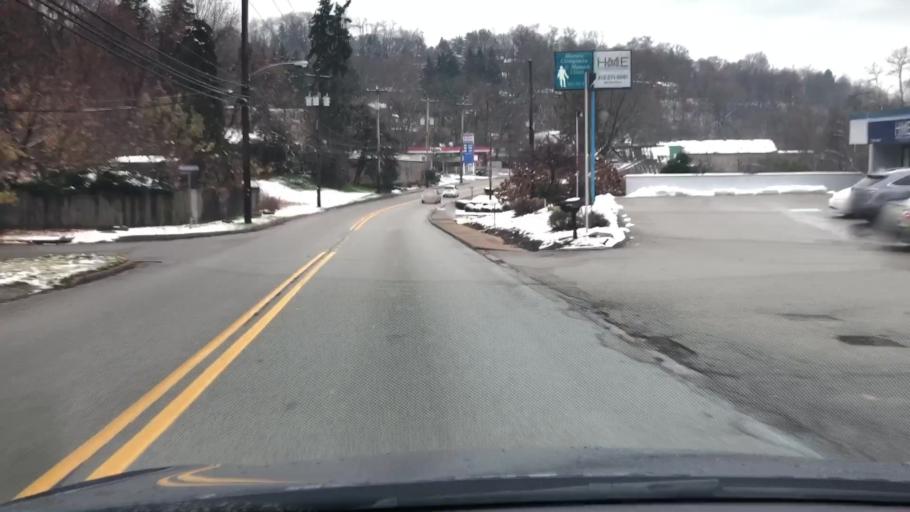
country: US
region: Pennsylvania
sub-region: Allegheny County
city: Churchill
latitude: 40.4567
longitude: -79.8232
